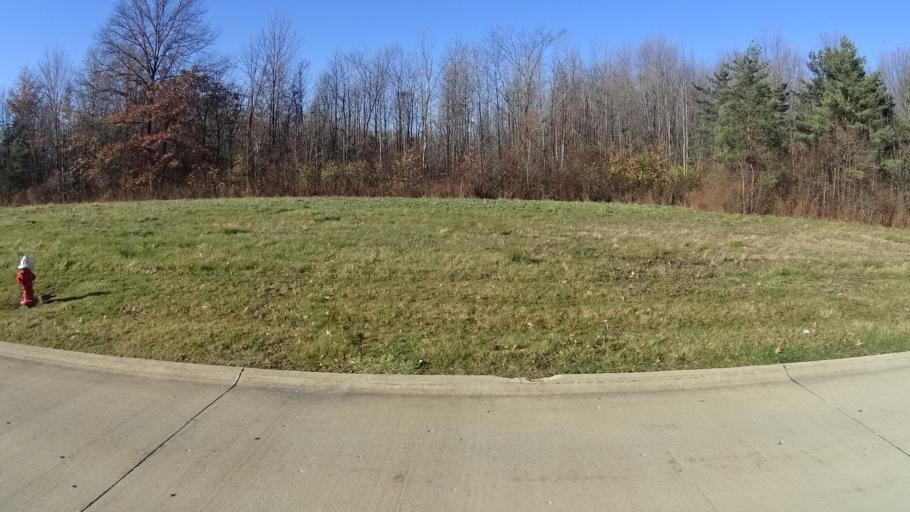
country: US
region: Ohio
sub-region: Lorain County
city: Avon
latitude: 41.4681
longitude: -82.0686
